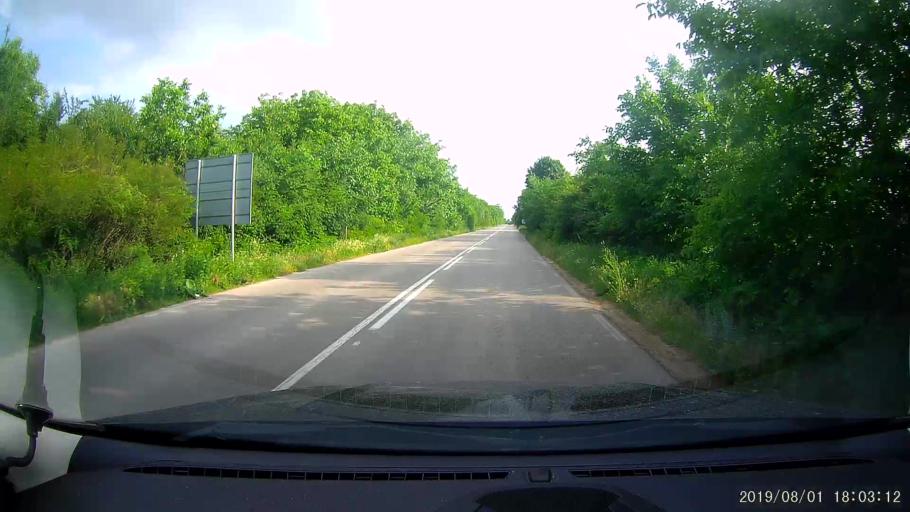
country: BG
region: Silistra
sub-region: Obshtina Alfatar
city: Alfatar
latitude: 43.9327
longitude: 27.2903
